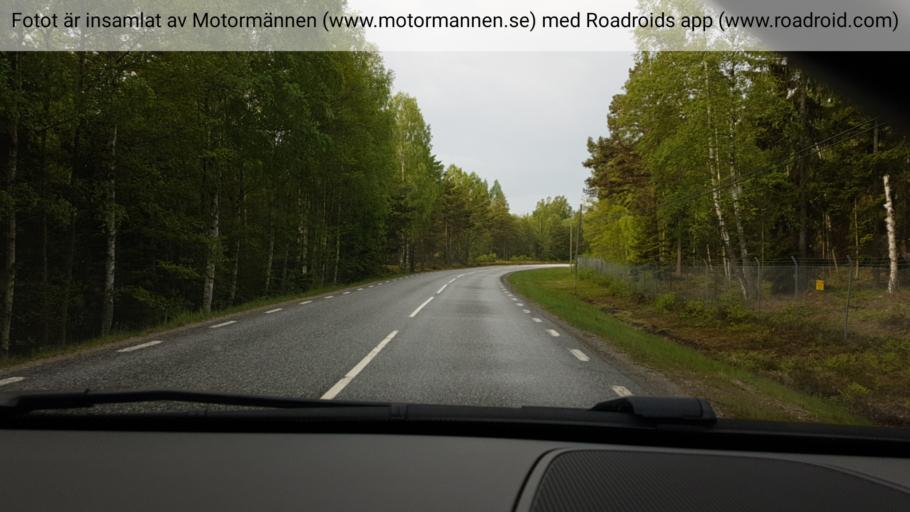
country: SE
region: Stockholm
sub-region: Nynashamns Kommun
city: Nynashamn
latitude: 58.9820
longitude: 18.0896
